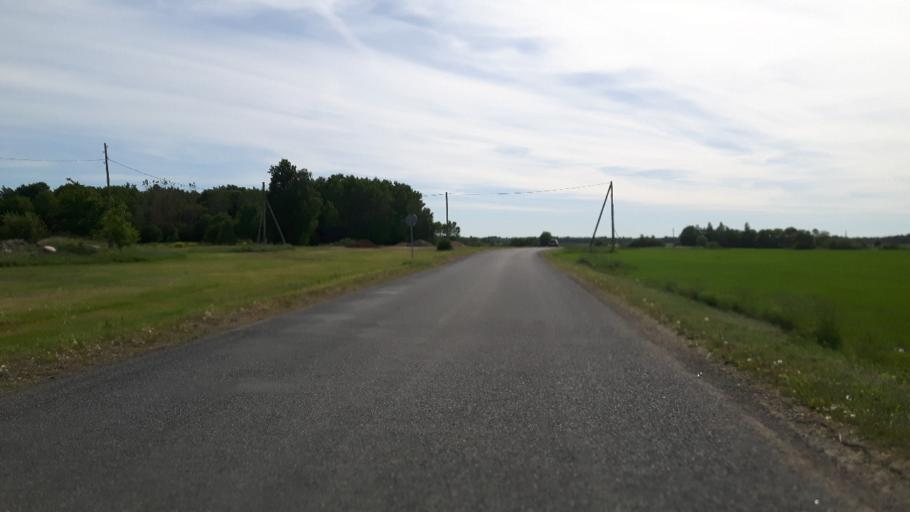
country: EE
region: Harju
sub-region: Raasiku vald
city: Arukula
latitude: 59.4243
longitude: 25.0873
